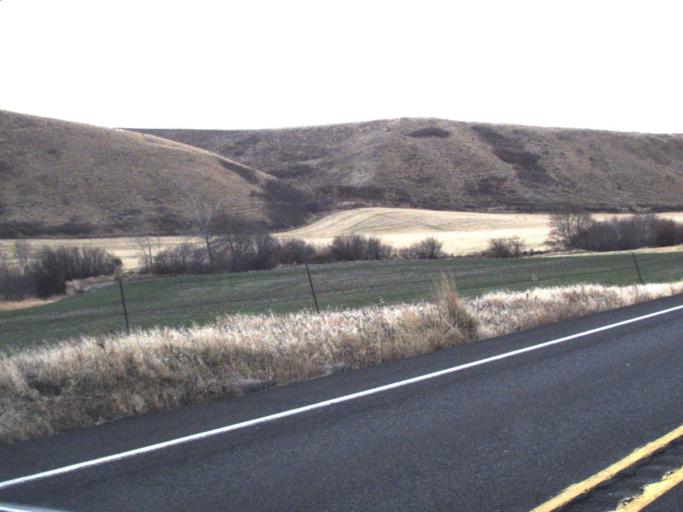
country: US
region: Washington
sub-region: Garfield County
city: Pomeroy
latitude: 46.4676
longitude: -117.5036
